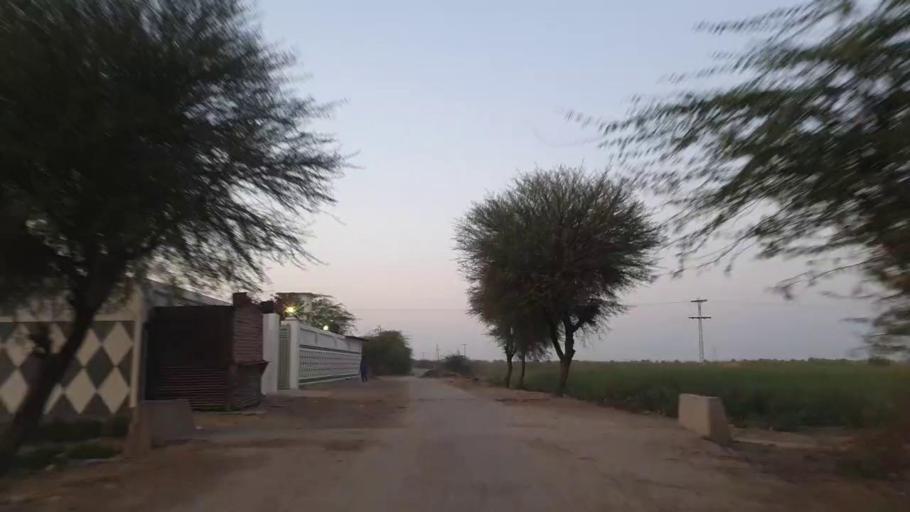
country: PK
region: Sindh
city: Naukot
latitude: 24.8878
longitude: 69.3853
